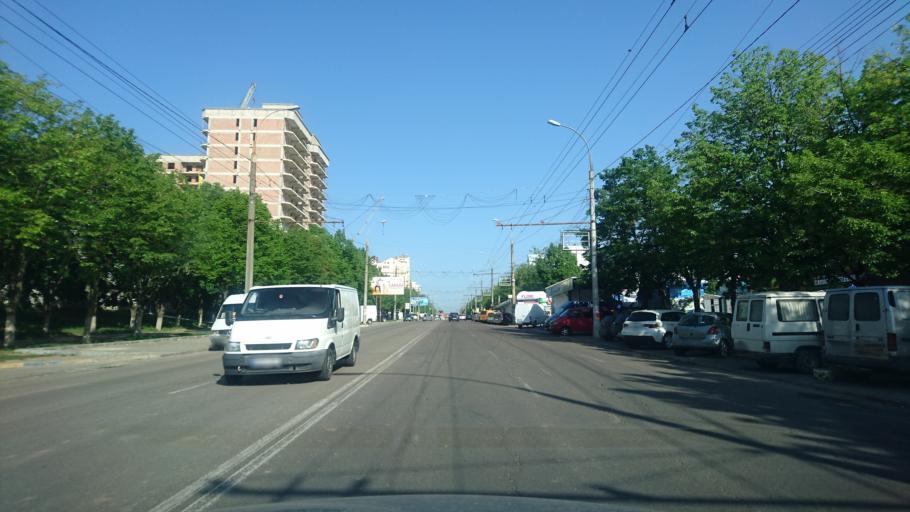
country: MD
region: Chisinau
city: Vatra
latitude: 47.0389
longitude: 28.7686
